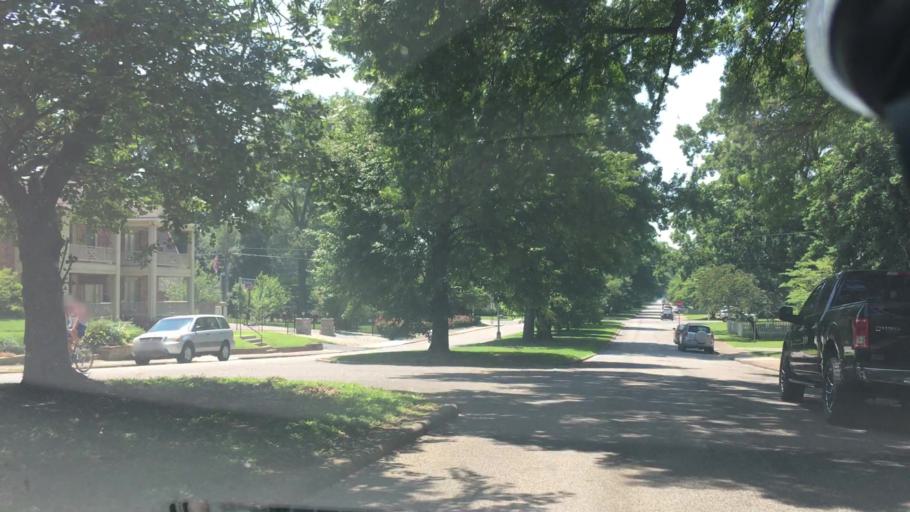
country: US
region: Indiana
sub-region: Vanderburgh County
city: Evansville
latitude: 37.9710
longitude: -87.5245
